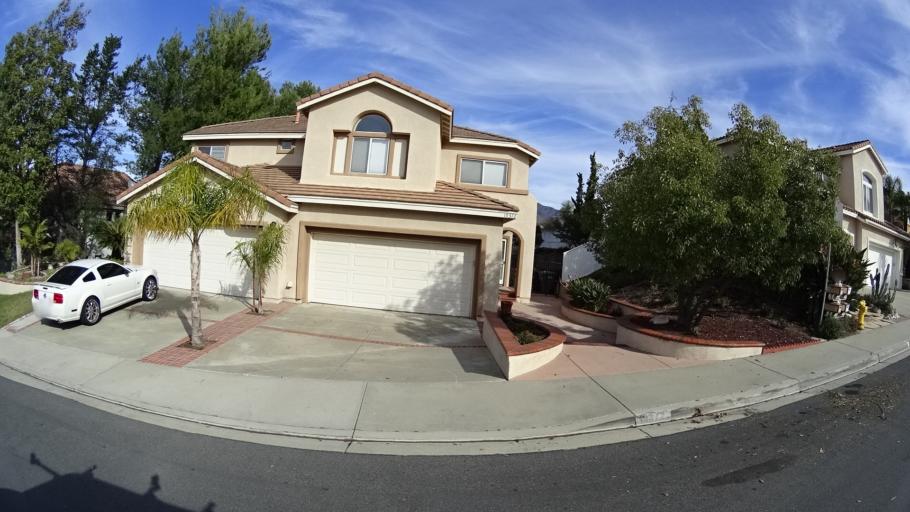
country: US
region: California
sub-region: Orange County
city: Portola Hills
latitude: 33.6807
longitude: -117.6293
